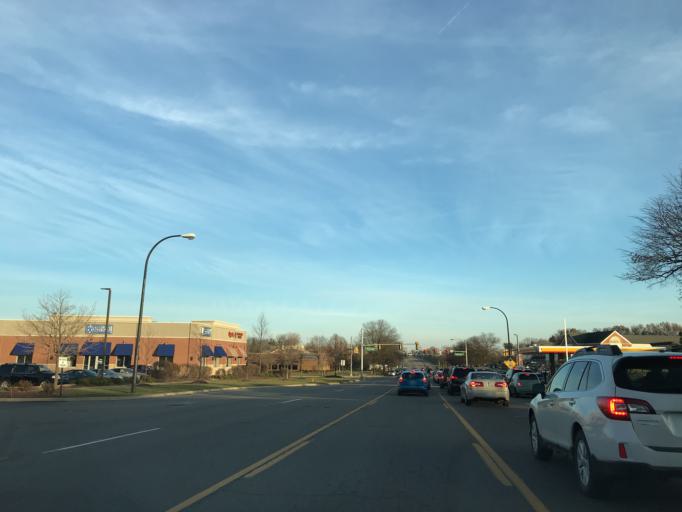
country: US
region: Michigan
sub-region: Washtenaw County
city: Ann Arbor
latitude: 42.2571
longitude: -83.6974
